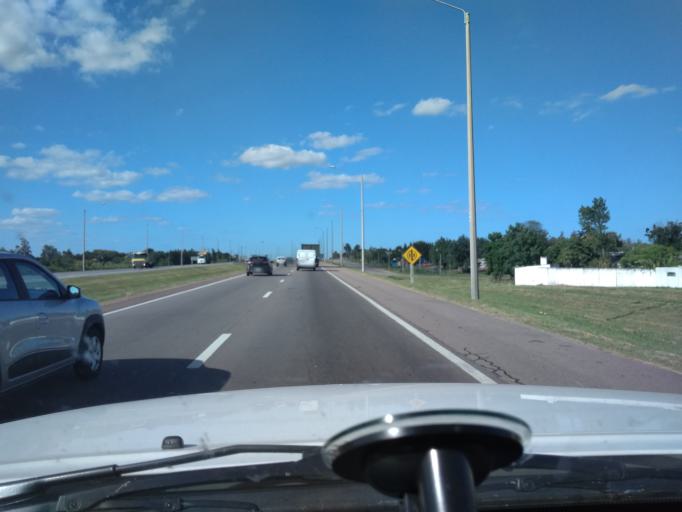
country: UY
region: Canelones
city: La Paz
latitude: -34.7717
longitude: -56.2688
